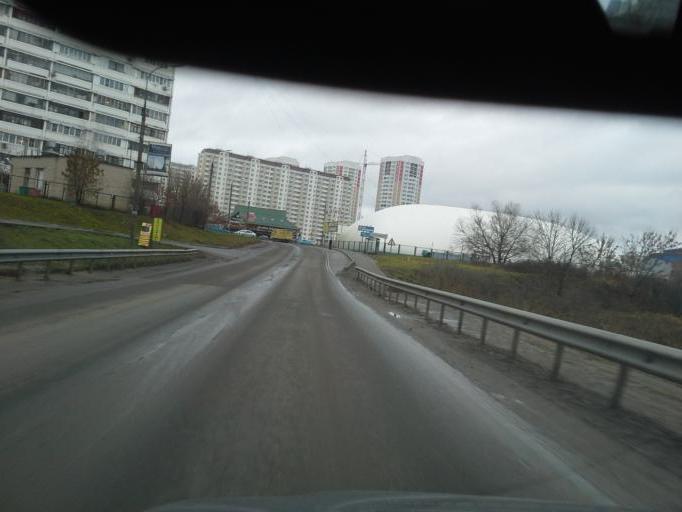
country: RU
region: Moskovskaya
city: Moskovskiy
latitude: 55.5964
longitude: 37.3543
